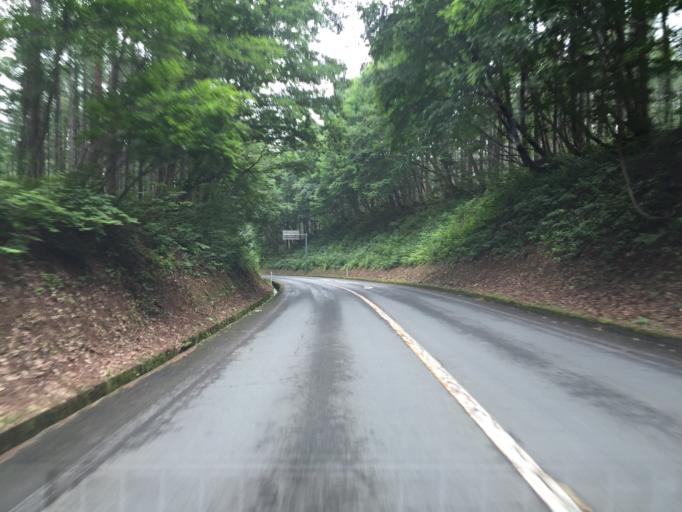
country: JP
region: Fukushima
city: Inawashiro
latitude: 37.6686
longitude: 140.1462
